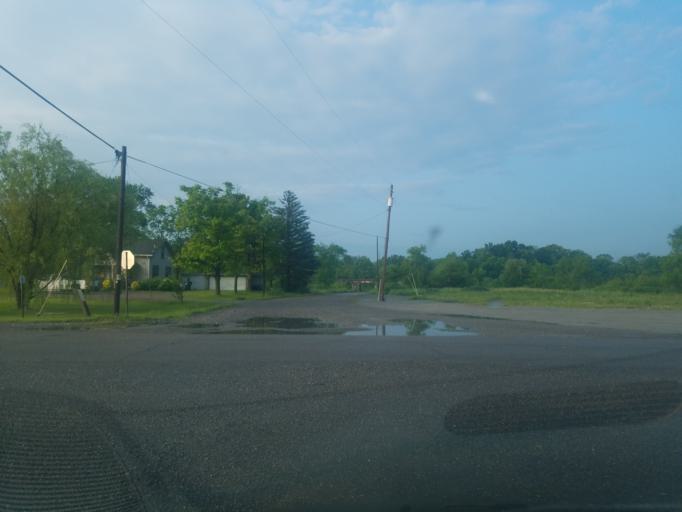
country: US
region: Ohio
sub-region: Stark County
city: Minerva
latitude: 40.7366
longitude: -80.9803
